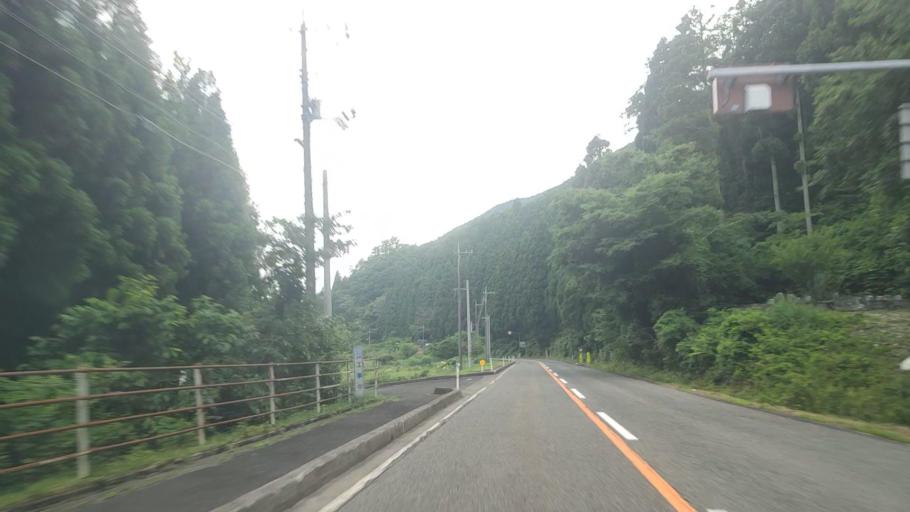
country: JP
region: Tottori
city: Kurayoshi
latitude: 35.3178
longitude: 133.8963
